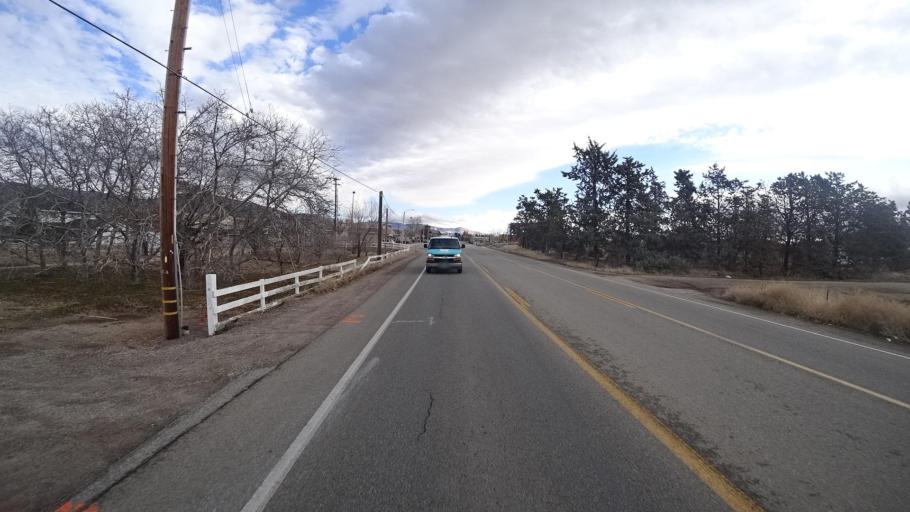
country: US
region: California
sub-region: Kern County
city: Tehachapi
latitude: 35.1247
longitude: -118.4711
